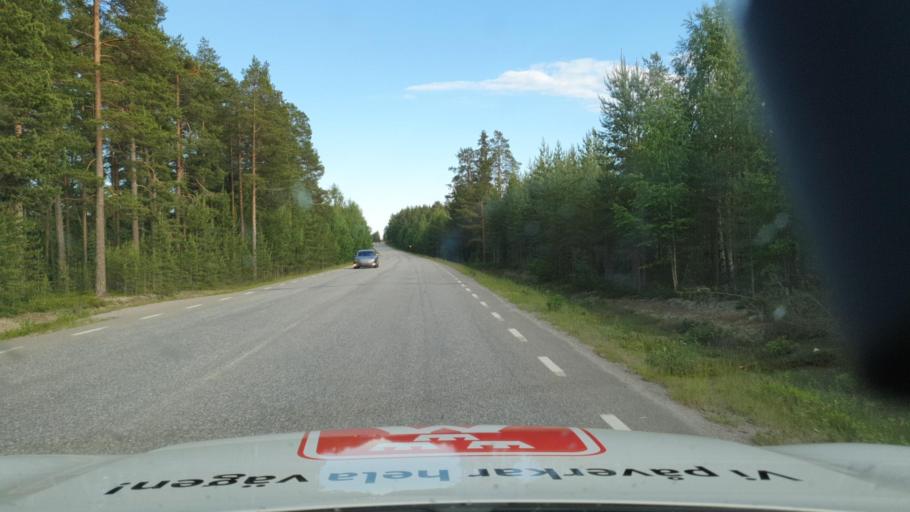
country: SE
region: Vaesterbotten
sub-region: Umea Kommun
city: Roback
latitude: 63.8532
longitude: 20.1503
